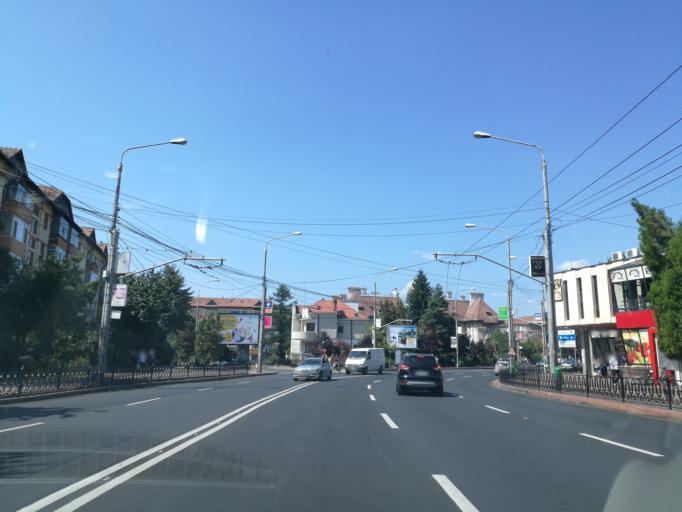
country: RO
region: Neamt
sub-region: Municipiul Piatra-Neamt
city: Valeni
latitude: 46.9272
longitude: 26.3713
